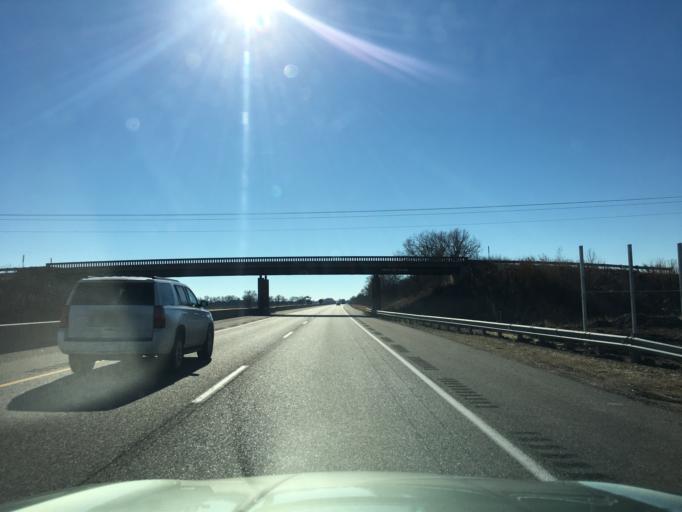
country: US
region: Kansas
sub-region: Sumner County
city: Belle Plaine
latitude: 37.4366
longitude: -97.3214
